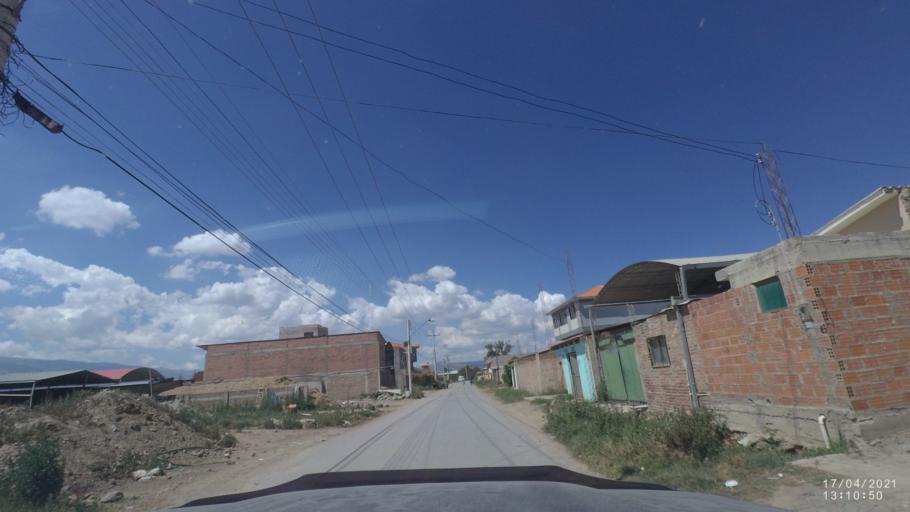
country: BO
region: Cochabamba
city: Cochabamba
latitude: -17.4144
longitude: -66.2224
